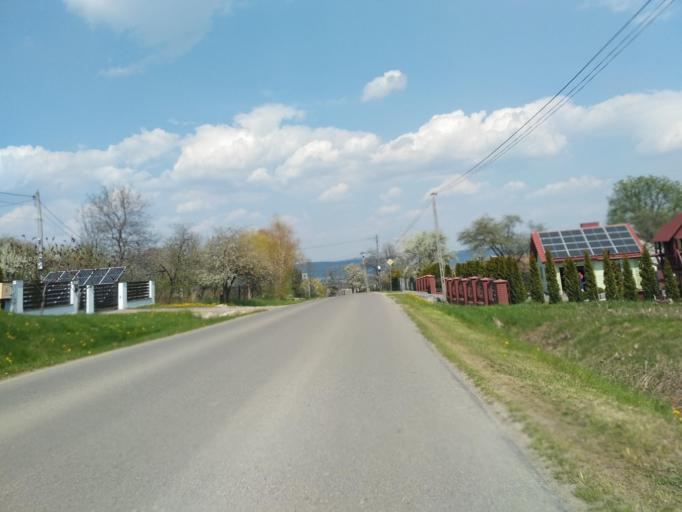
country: PL
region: Subcarpathian Voivodeship
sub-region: Powiat jasielski
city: Jaslo
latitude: 49.7118
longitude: 21.5066
